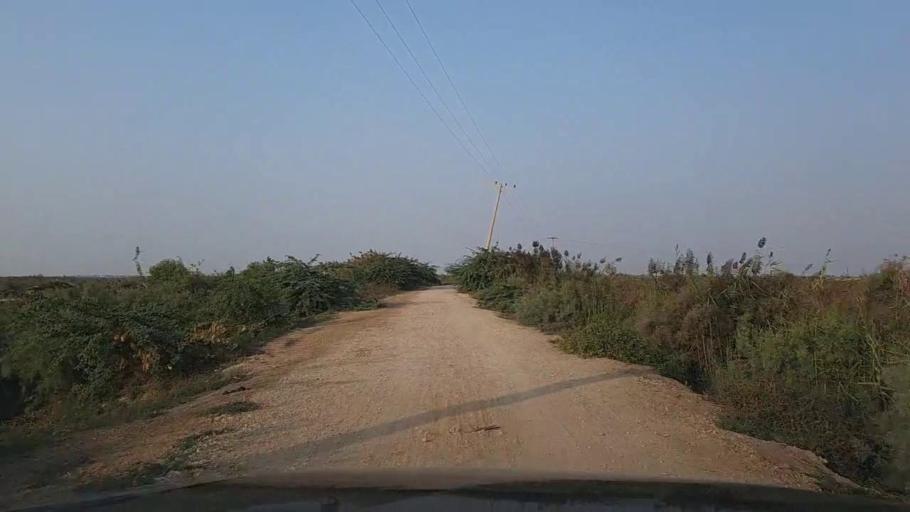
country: PK
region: Sindh
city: Mirpur Sakro
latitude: 24.4158
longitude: 67.7328
